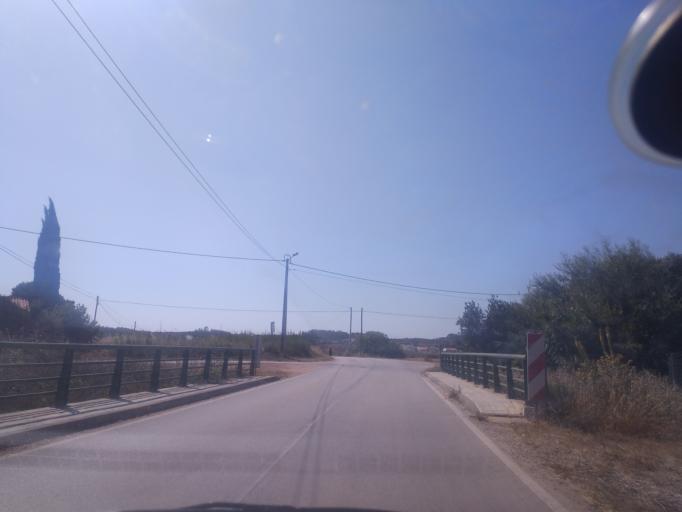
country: PT
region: Faro
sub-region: Aljezur
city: Aljezur
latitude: 37.2277
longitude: -8.8236
